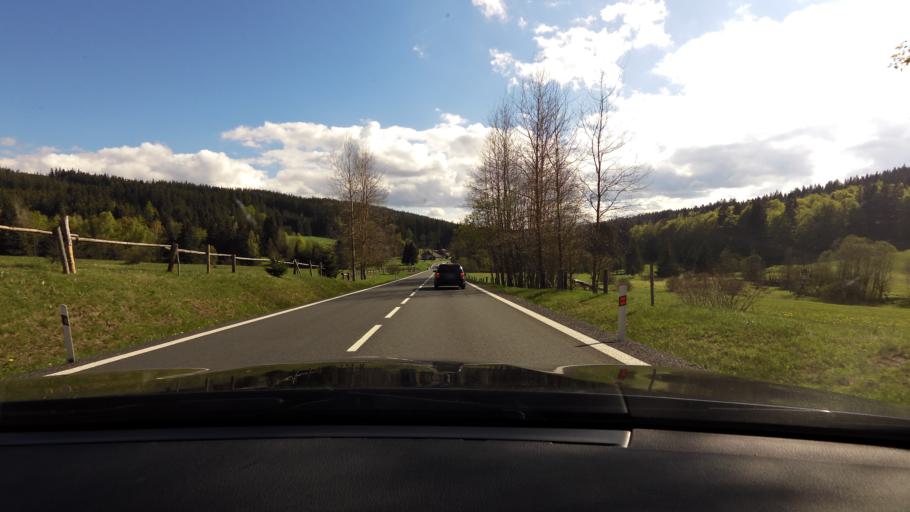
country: CZ
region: Plzensky
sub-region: Okres Klatovy
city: Zelezna Ruda
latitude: 49.1523
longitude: 13.2582
